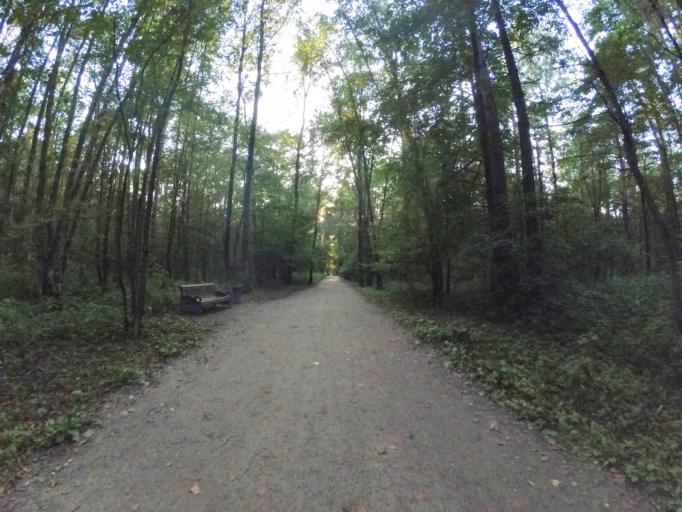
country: RU
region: Moscow
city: Khimki
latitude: 55.8689
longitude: 37.4180
